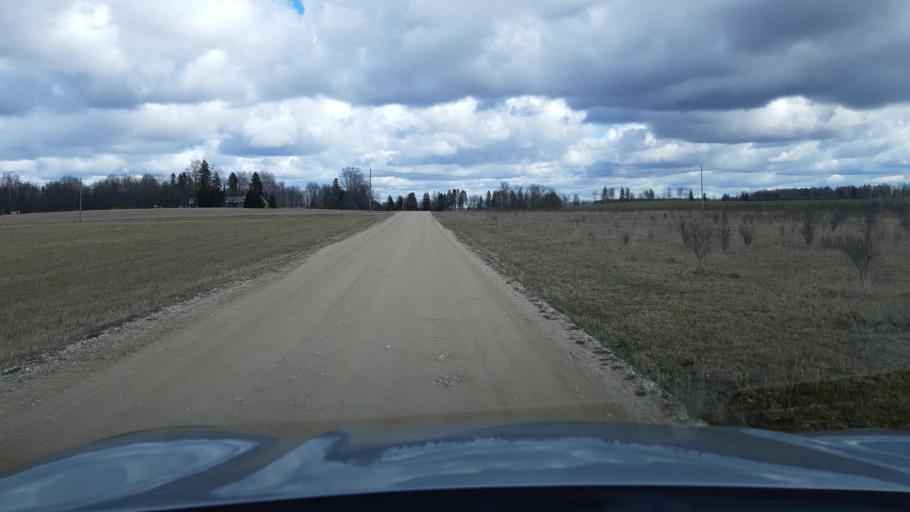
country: EE
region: Harju
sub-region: Rae vald
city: Vaida
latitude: 59.0764
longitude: 25.1107
